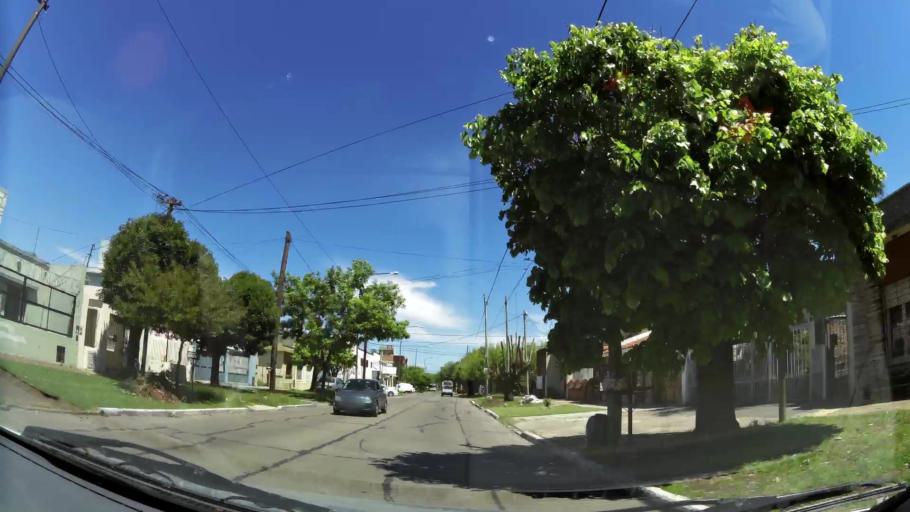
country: AR
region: Buenos Aires
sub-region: Partido de Quilmes
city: Quilmes
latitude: -34.7283
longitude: -58.2706
